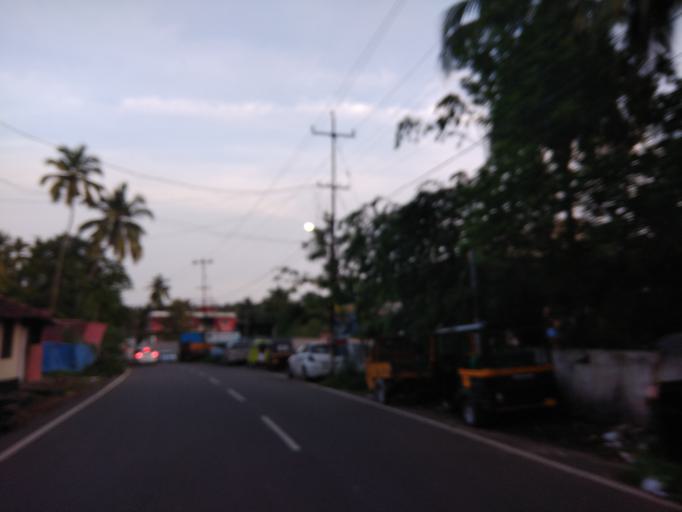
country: IN
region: Kerala
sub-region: Thrissur District
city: Trichur
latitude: 10.5204
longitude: 76.2023
